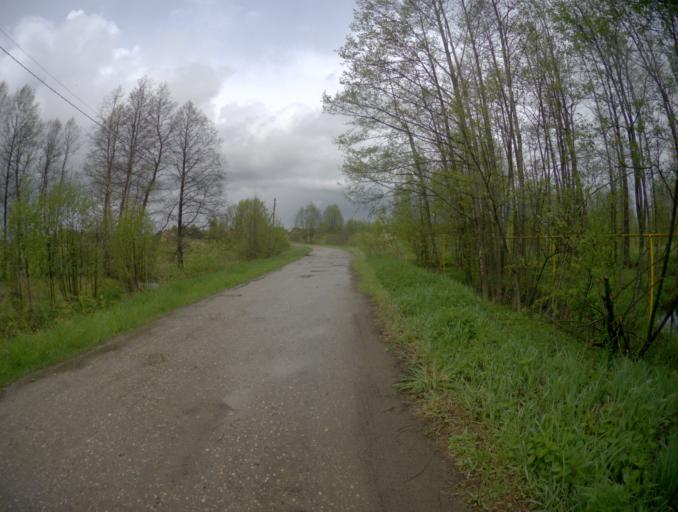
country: RU
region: Vladimir
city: Velikodvorskiy
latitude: 55.3707
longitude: 40.8596
